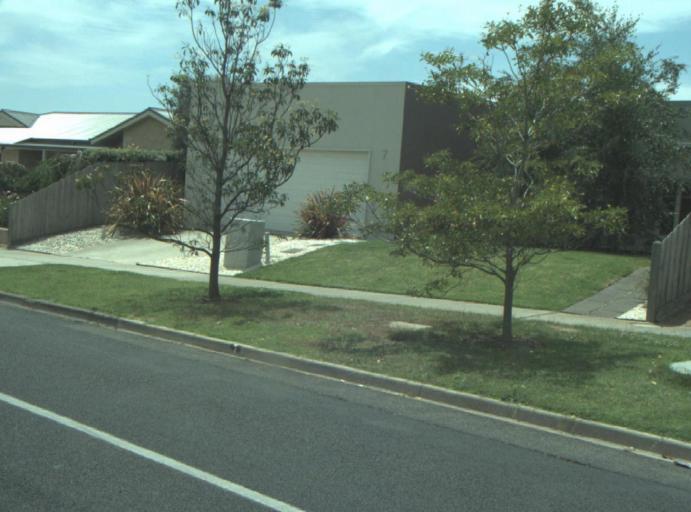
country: AU
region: Victoria
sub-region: Greater Geelong
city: Clifton Springs
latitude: -38.1619
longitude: 144.5684
